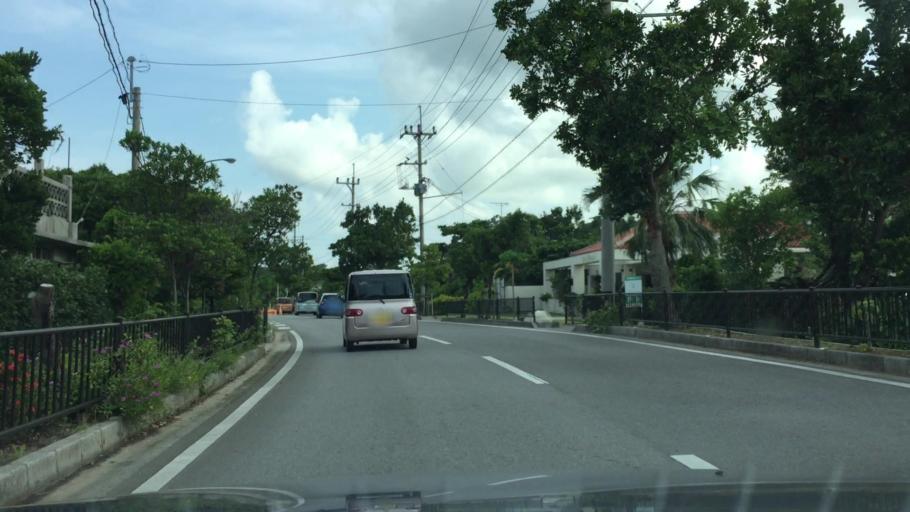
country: JP
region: Okinawa
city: Ishigaki
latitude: 24.4558
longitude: 124.2484
